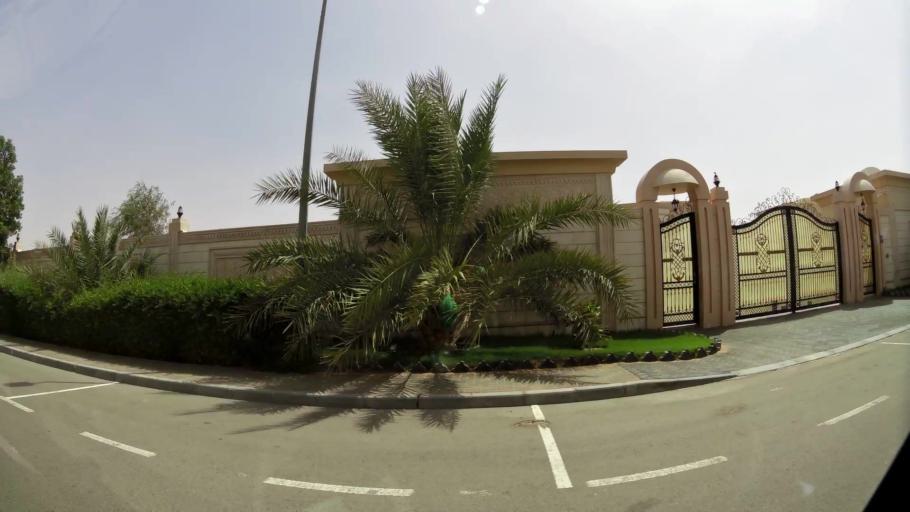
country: AE
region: Abu Dhabi
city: Al Ain
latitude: 24.1527
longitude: 55.6488
